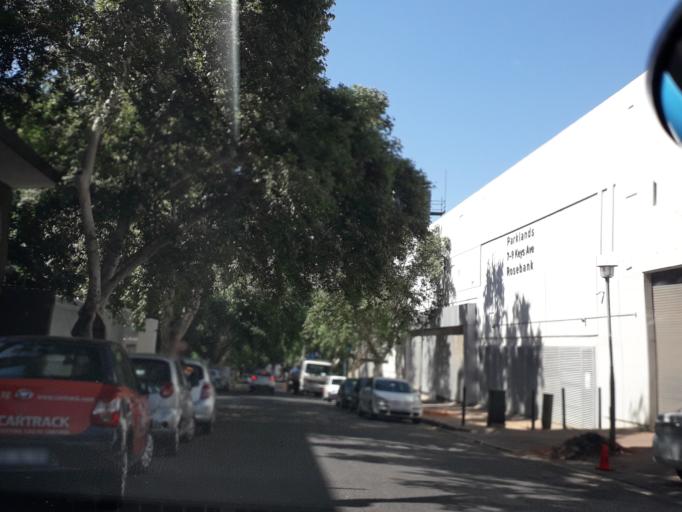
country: ZA
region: Gauteng
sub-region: City of Johannesburg Metropolitan Municipality
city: Johannesburg
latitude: -26.1461
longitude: 28.0370
